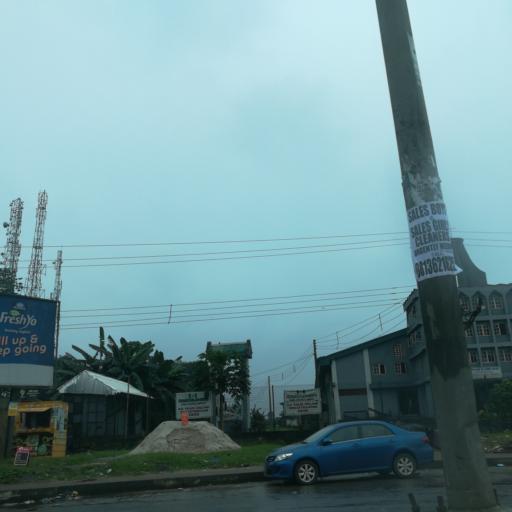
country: NG
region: Rivers
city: Port Harcourt
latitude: 4.7923
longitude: 6.9973
